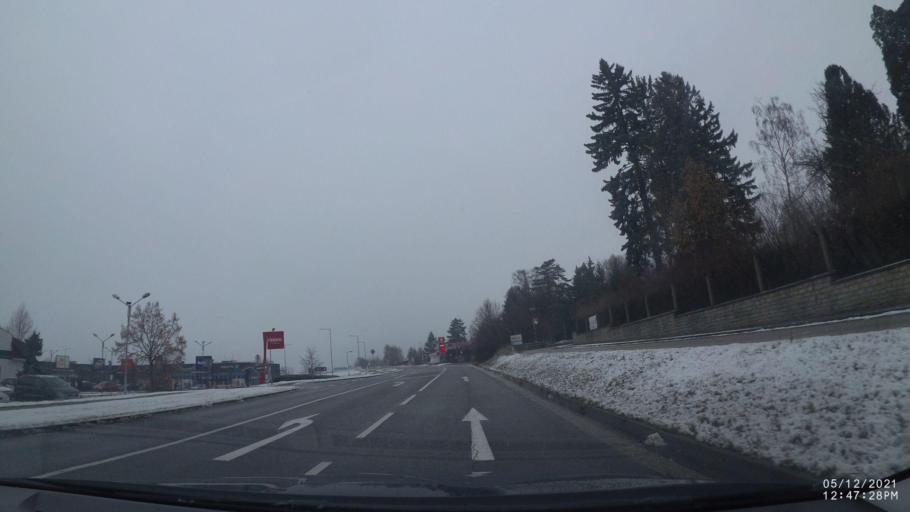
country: CZ
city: Nove Mesto nad Metuji
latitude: 50.3588
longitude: 16.1485
